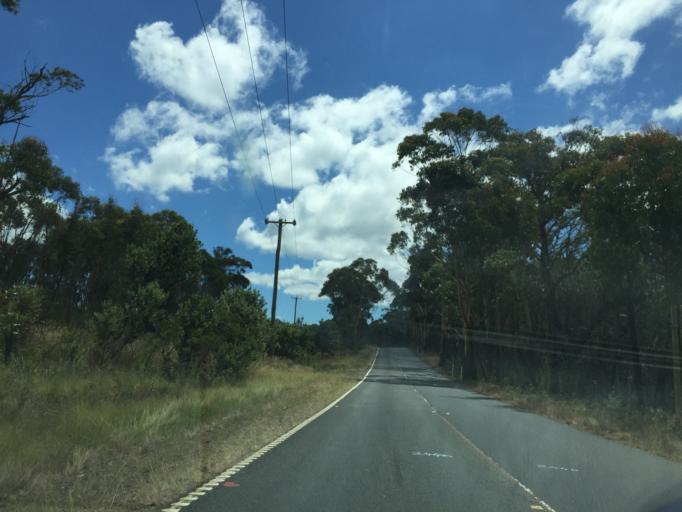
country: AU
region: New South Wales
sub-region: Blue Mountains Municipality
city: Blackheath
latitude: -33.5375
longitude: 150.3269
